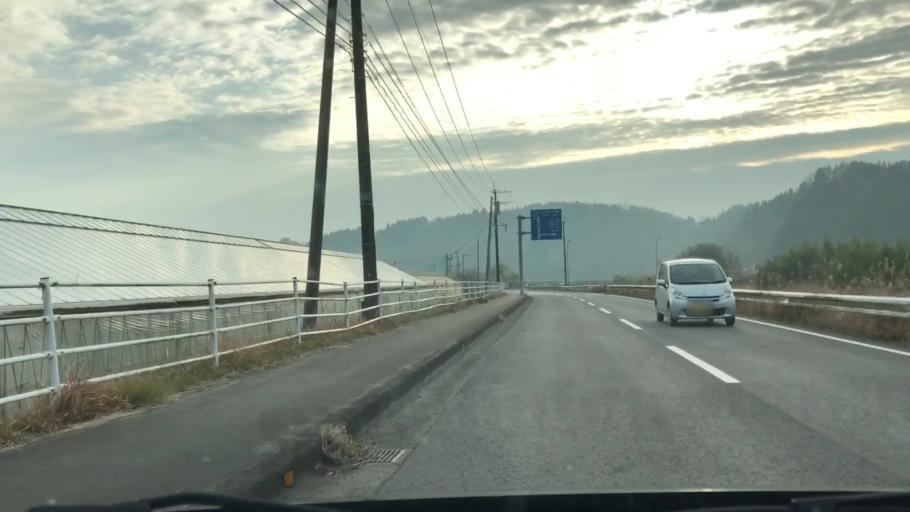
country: JP
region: Oita
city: Takedamachi
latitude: 32.9655
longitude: 131.4825
